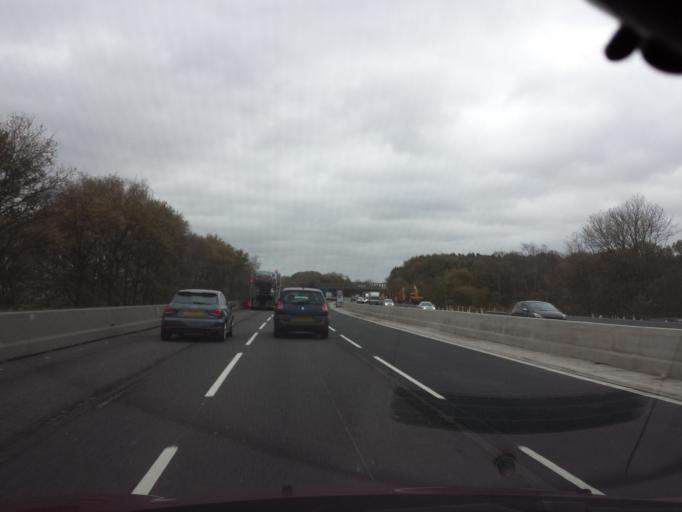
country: GB
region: England
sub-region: Surrey
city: Windlesham
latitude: 51.3588
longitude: -0.6706
